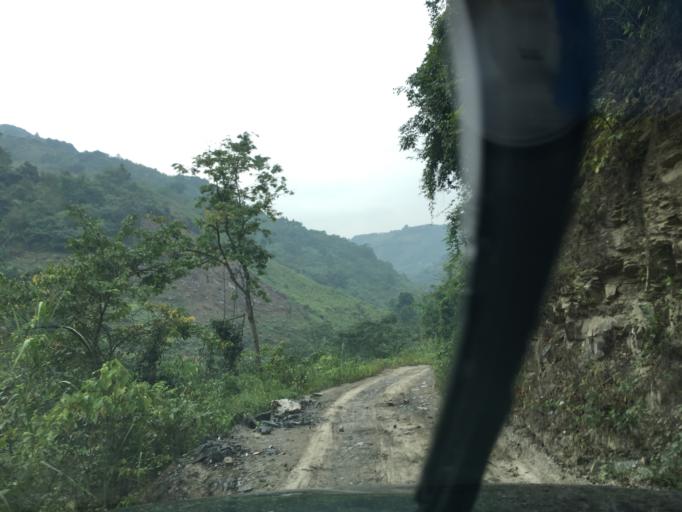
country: CN
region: Guangxi Zhuangzu Zizhiqu
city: Xinzhou
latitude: 25.0518
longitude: 105.9199
